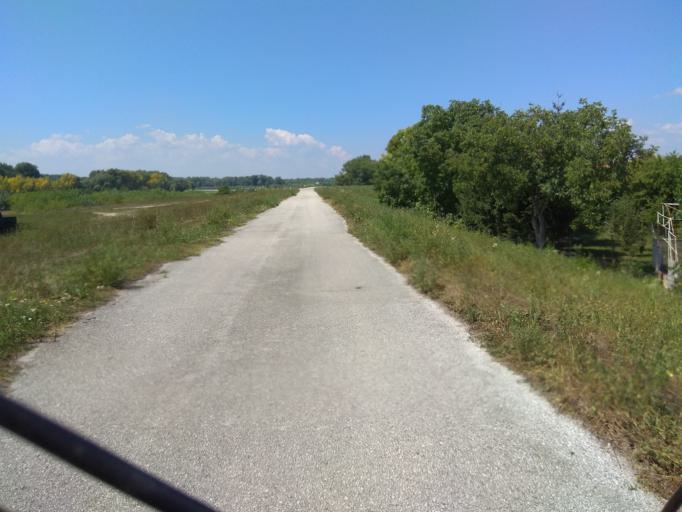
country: SK
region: Trnavsky
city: Gabcikovo
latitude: 47.8180
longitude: 17.6169
